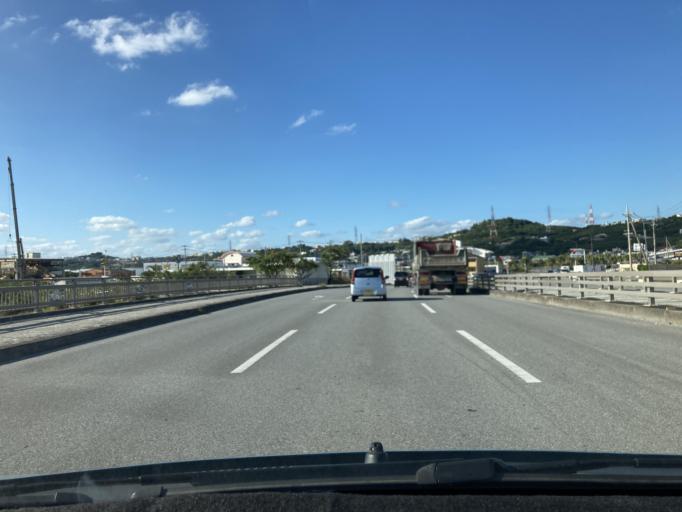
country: JP
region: Okinawa
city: Katsuren-haebaru
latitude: 26.3425
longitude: 127.8568
